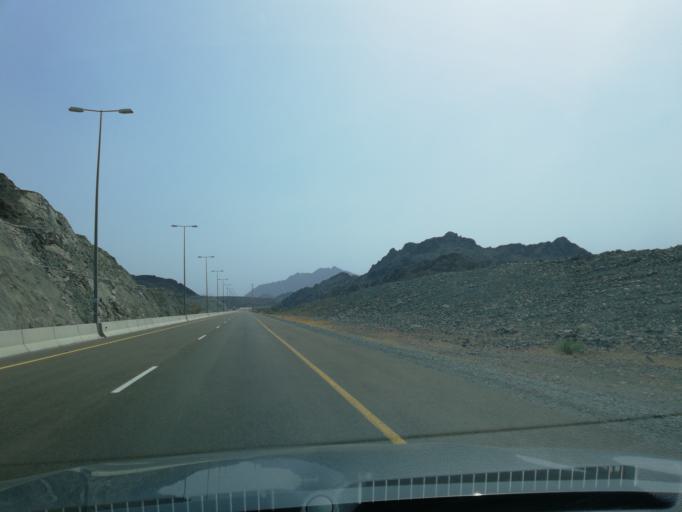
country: OM
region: Al Batinah
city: Al Liwa'
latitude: 24.2665
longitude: 56.3857
